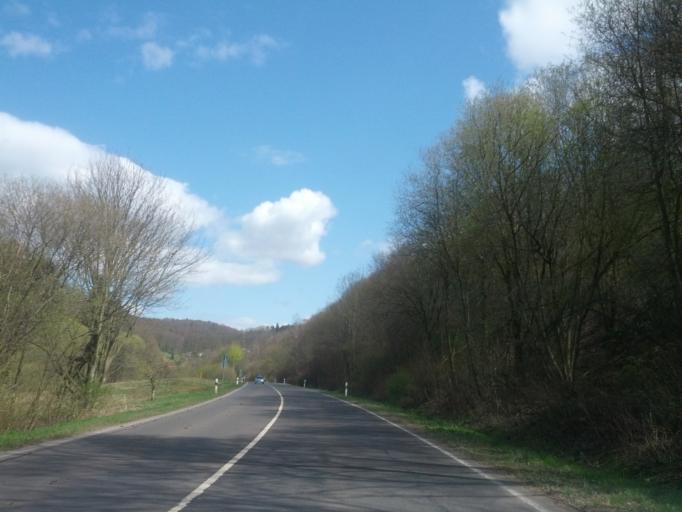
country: DE
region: Thuringia
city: Seebach
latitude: 50.9149
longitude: 10.4044
